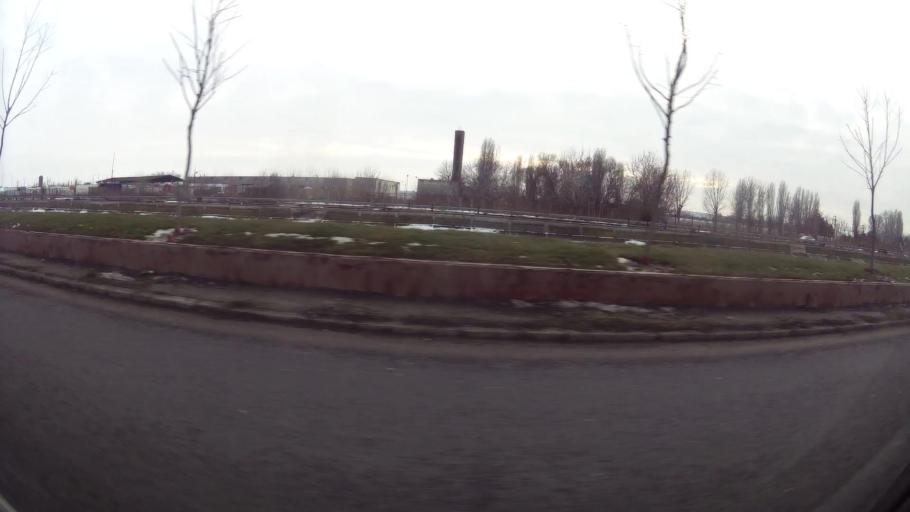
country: RO
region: Ilfov
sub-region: Comuna Popesti-Leordeni
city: Popesti-Leordeni
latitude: 44.3962
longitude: 26.1724
